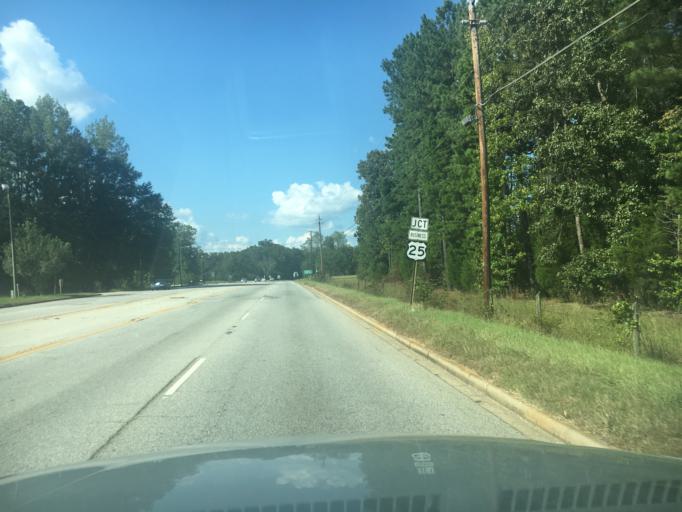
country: US
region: South Carolina
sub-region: Greenwood County
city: Ware Shoals
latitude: 34.3755
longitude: -82.2239
